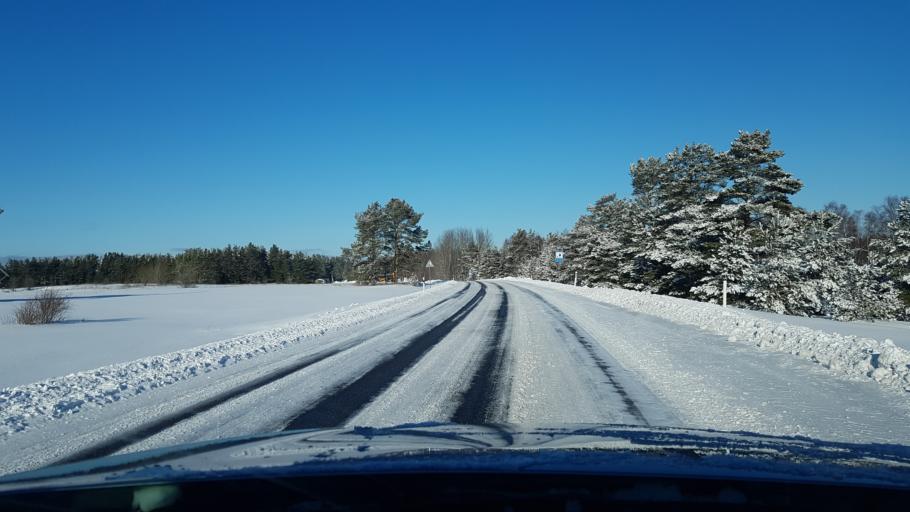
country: EE
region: Hiiumaa
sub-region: Kaerdla linn
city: Kardla
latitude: 58.9570
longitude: 22.7734
